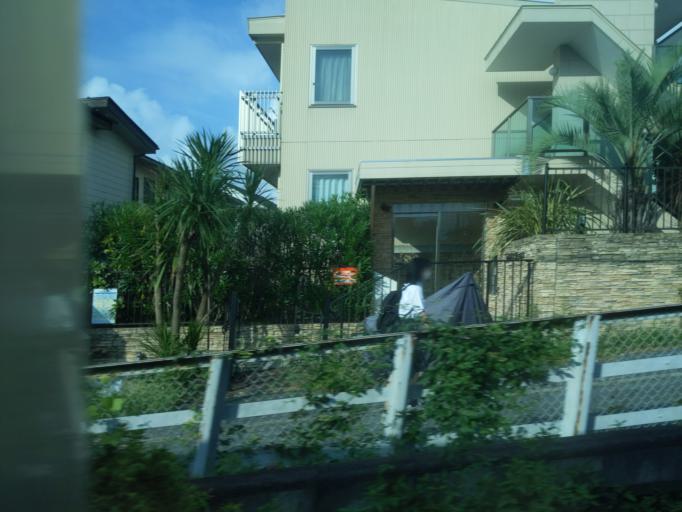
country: JP
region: Tokyo
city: Musashino
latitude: 35.6953
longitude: 139.5854
